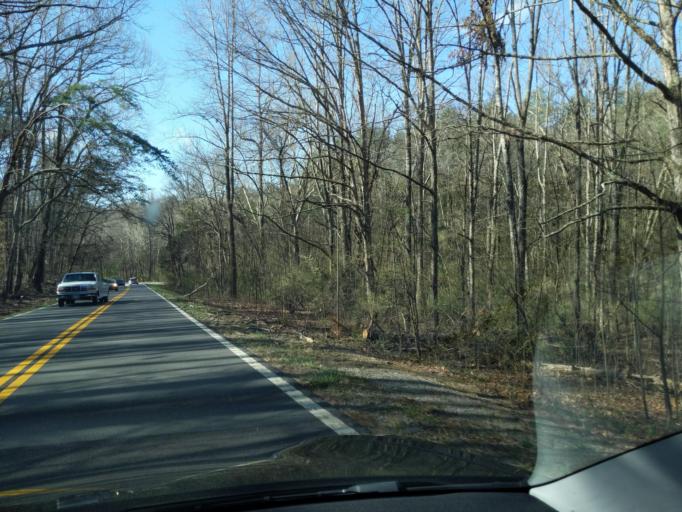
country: US
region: Tennessee
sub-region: Sevier County
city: Sevierville
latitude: 35.9641
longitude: -83.5487
